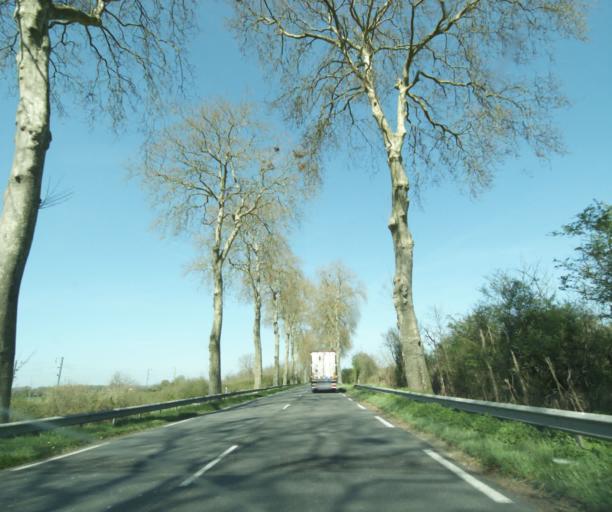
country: FR
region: Bourgogne
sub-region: Departement de la Nievre
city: Chantenay-Saint-Imbert
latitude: 46.7199
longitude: 3.1830
